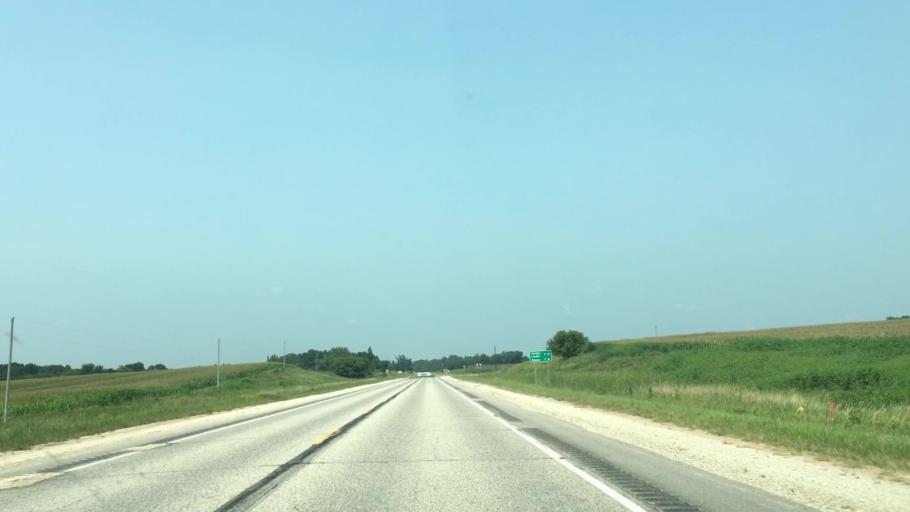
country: US
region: Iowa
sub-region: Fayette County
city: Fayette
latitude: 42.8152
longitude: -91.8051
